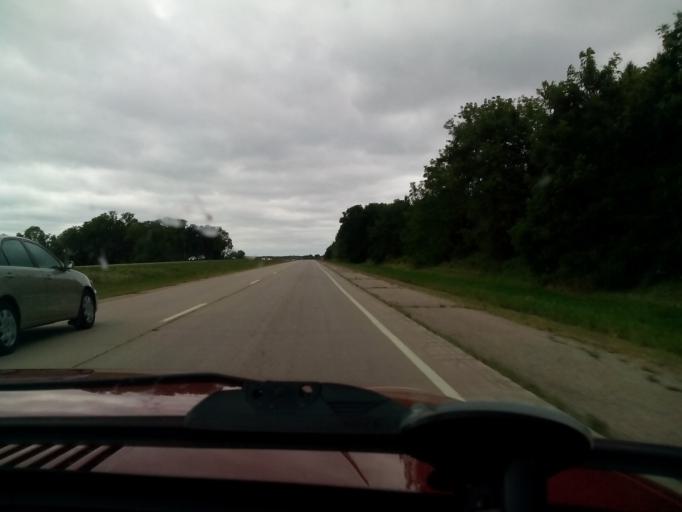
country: US
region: Wisconsin
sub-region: Dane County
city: Marshall
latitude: 43.2506
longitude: -89.1325
